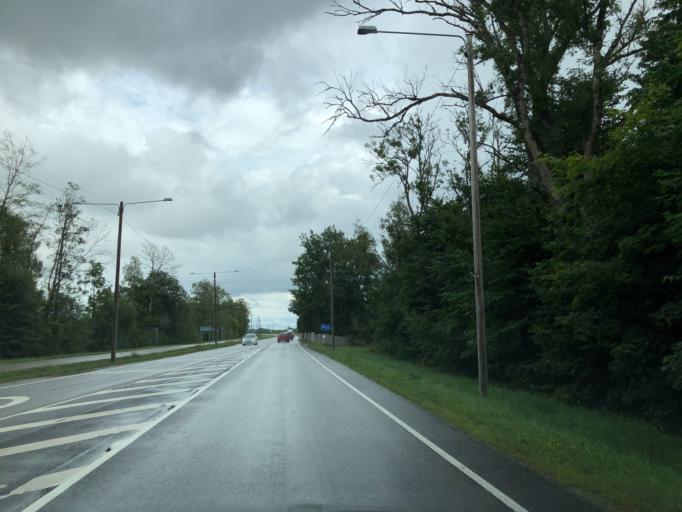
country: EE
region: Laeaene
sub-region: Ridala Parish
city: Uuemoisa
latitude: 58.9563
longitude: 23.7487
